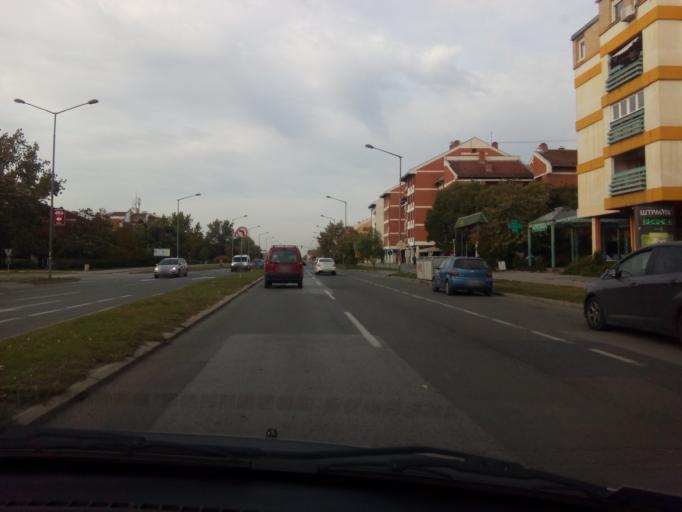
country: RS
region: Autonomna Pokrajina Vojvodina
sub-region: Juznobacki Okrug
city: Novi Sad
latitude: 45.2536
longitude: 19.8040
